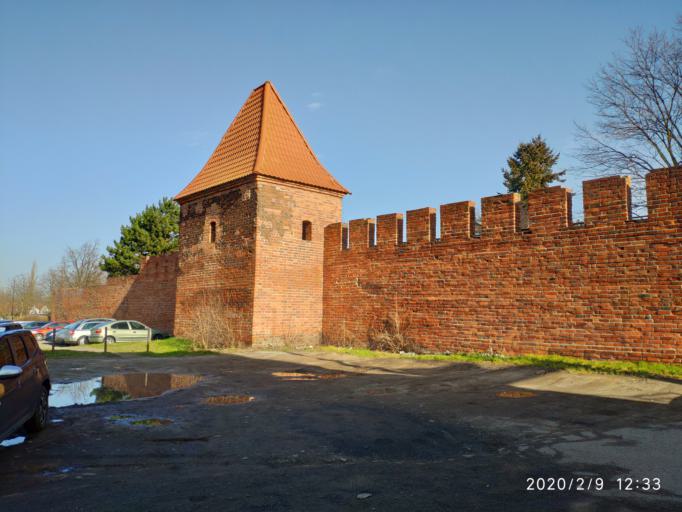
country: PL
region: Lower Silesian Voivodeship
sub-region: Powiat glogowski
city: Glogow
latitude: 51.6653
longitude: 16.0880
